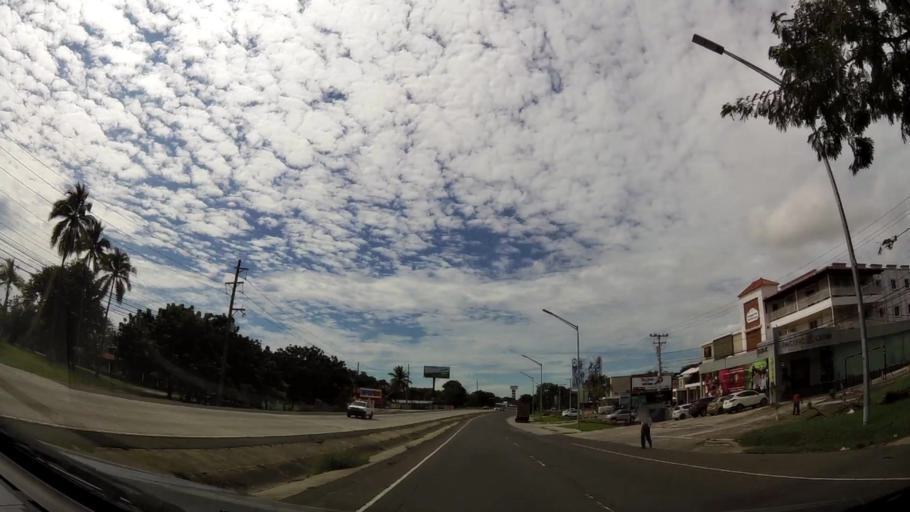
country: PA
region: Panama
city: Nueva Gorgona
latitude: 8.5411
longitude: -79.9152
